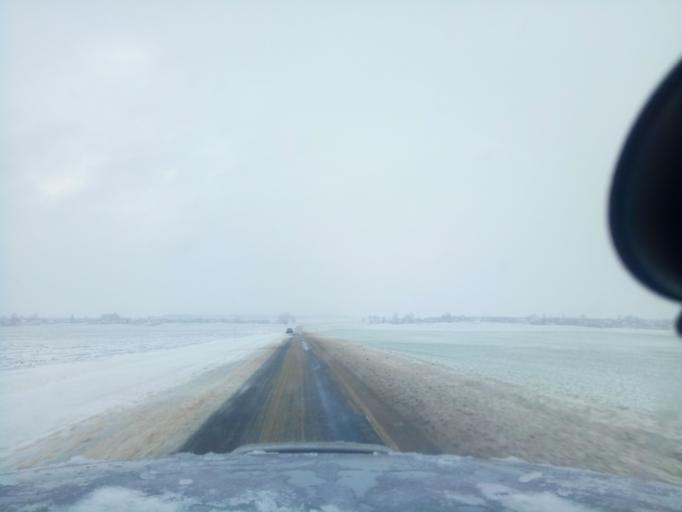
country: BY
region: Minsk
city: Haradzyeya
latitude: 53.3061
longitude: 26.5713
